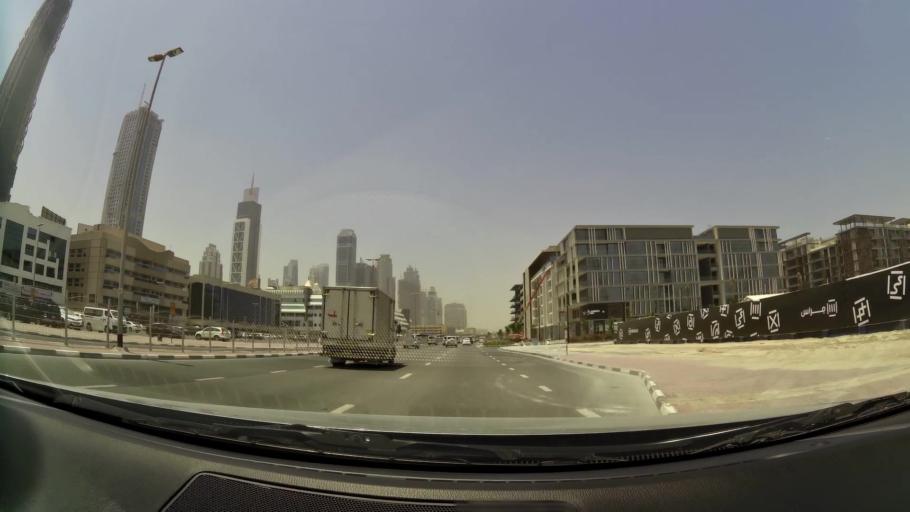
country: AE
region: Dubai
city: Dubai
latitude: 25.2018
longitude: 55.2662
